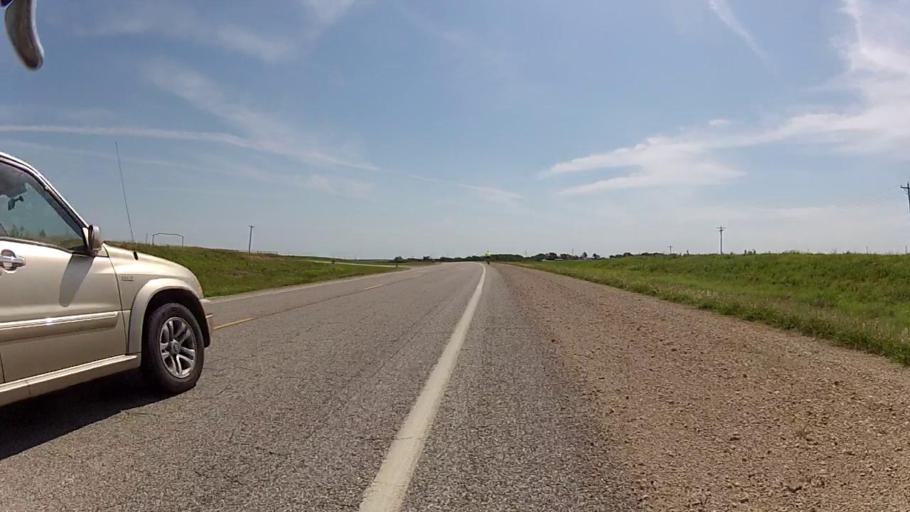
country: US
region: Kansas
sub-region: Chautauqua County
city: Sedan
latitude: 37.1103
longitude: -96.5149
